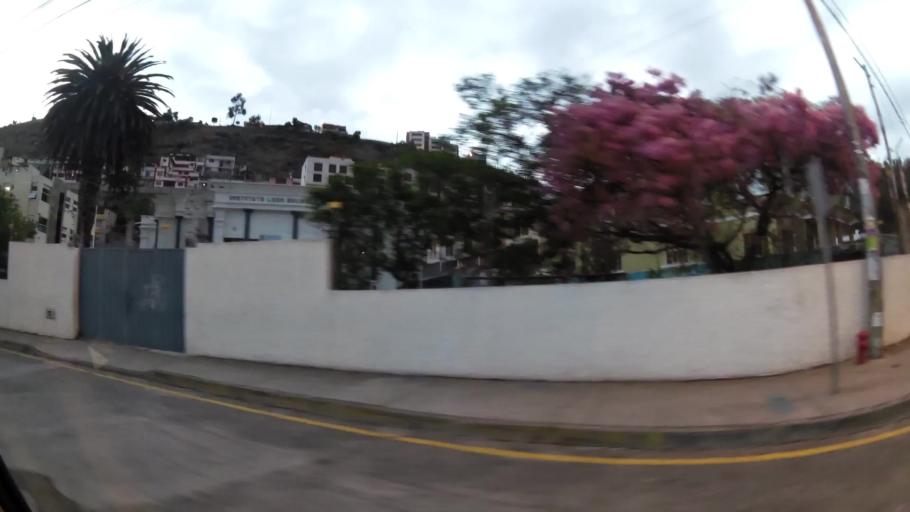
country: EC
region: Tungurahua
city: Ambato
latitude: -1.2513
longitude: -78.6403
